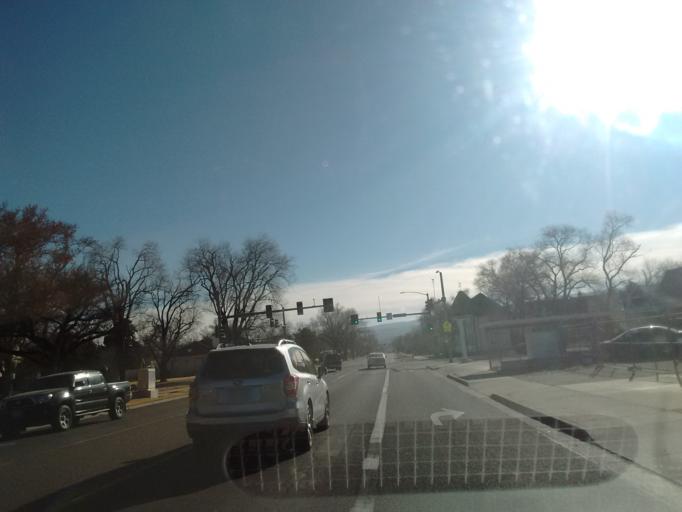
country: US
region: Colorado
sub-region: Mesa County
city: Grand Junction
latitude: 39.0739
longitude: -108.5524
